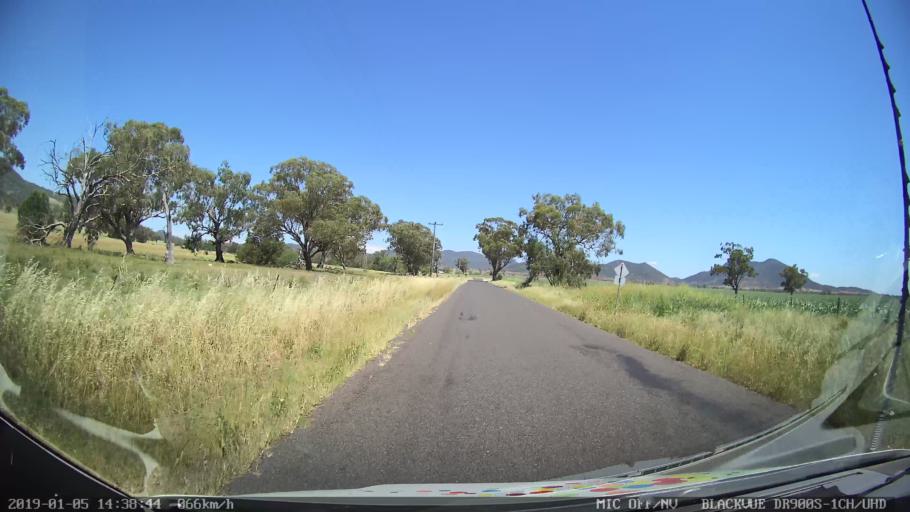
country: AU
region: New South Wales
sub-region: Tamworth Municipality
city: Phillip
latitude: -31.2509
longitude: 150.6937
